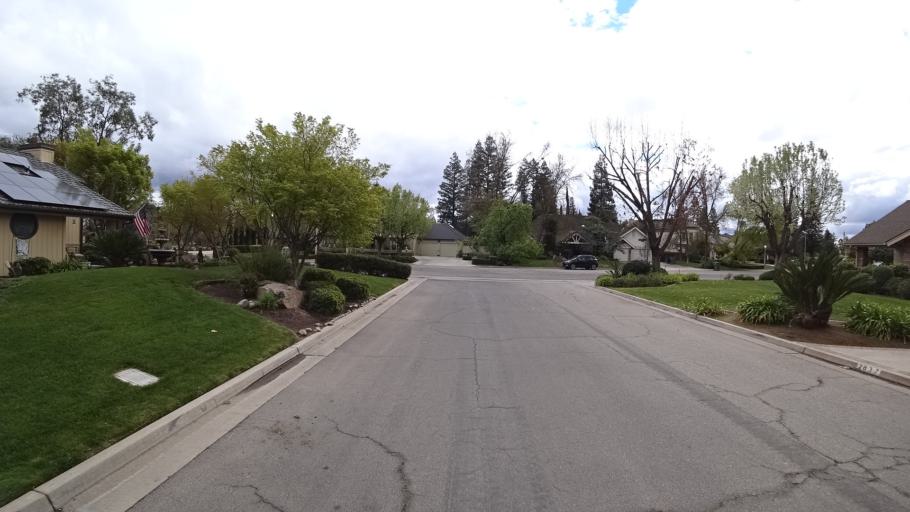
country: US
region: California
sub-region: Fresno County
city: Fresno
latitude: 36.8487
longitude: -119.8453
